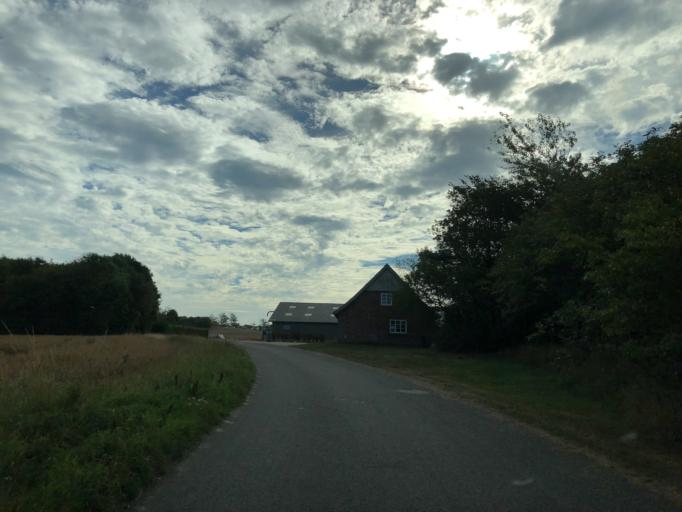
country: DK
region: Central Jutland
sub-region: Ringkobing-Skjern Kommune
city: Skjern
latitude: 56.0419
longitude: 8.4389
